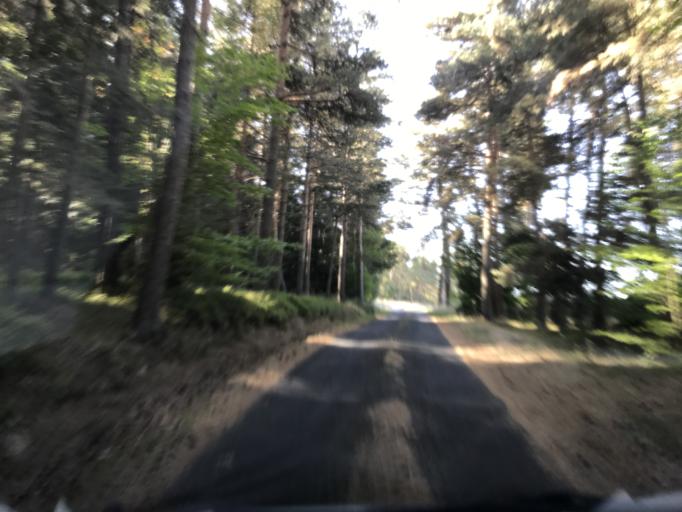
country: FR
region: Rhone-Alpes
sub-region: Departement de l'Ardeche
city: Saint-Agreve
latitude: 45.0358
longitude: 4.4440
